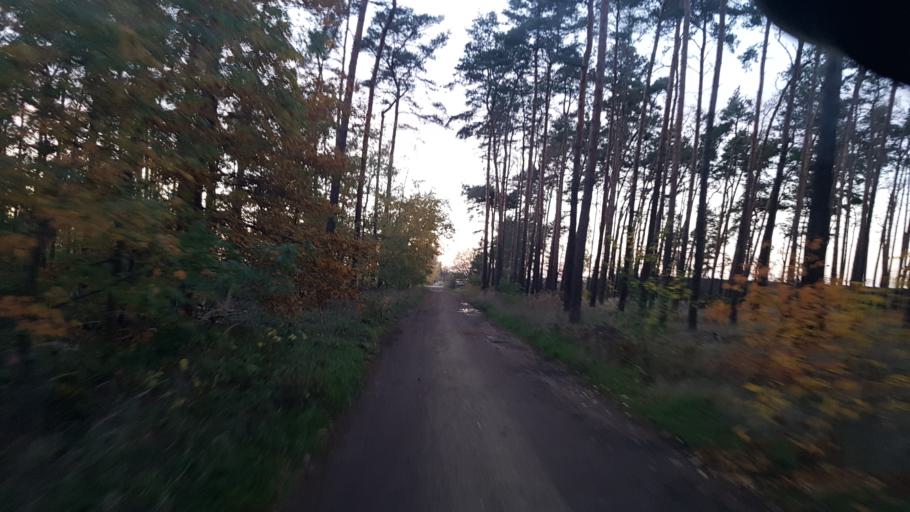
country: DE
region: Brandenburg
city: Bad Liebenwerda
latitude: 51.5085
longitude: 13.3177
